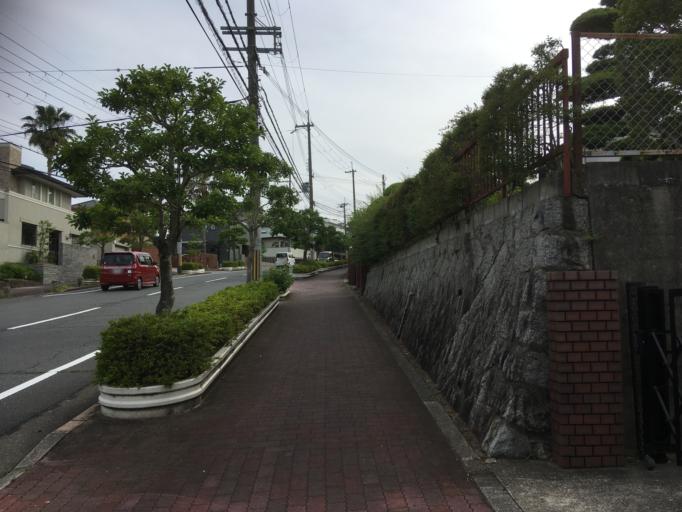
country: JP
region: Nara
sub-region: Ikoma-shi
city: Ikoma
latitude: 34.6904
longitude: 135.7290
